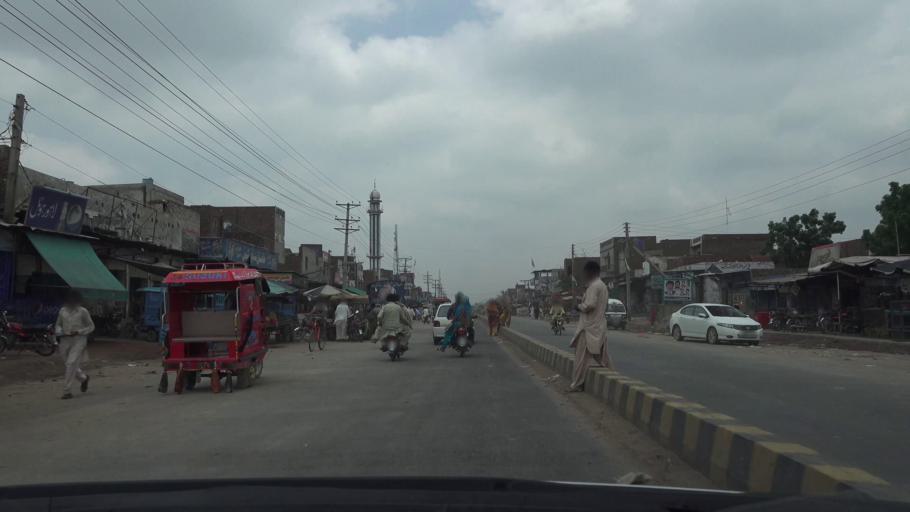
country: PK
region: Punjab
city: Faisalabad
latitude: 31.3894
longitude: 73.1938
